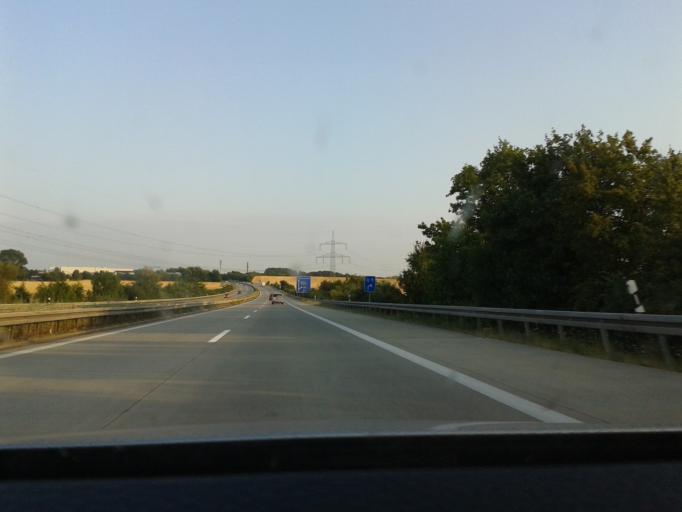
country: DE
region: Saxony
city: Mochau
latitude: 51.1218
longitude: 13.1708
